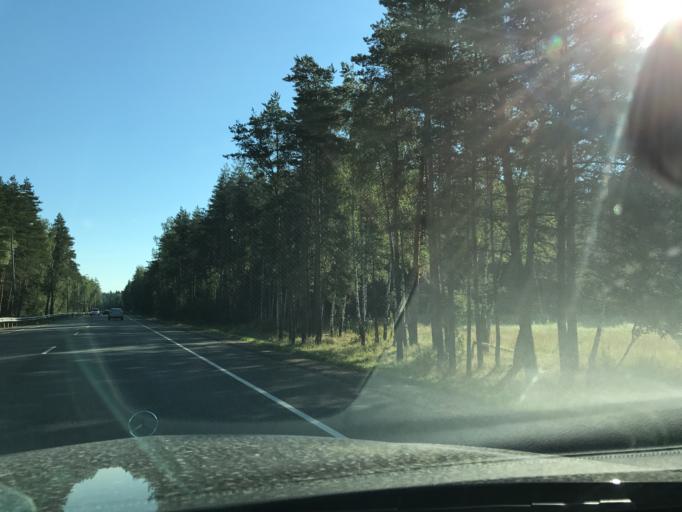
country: RU
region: Moskovskaya
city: Chernogolovka
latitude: 55.9672
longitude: 38.2875
